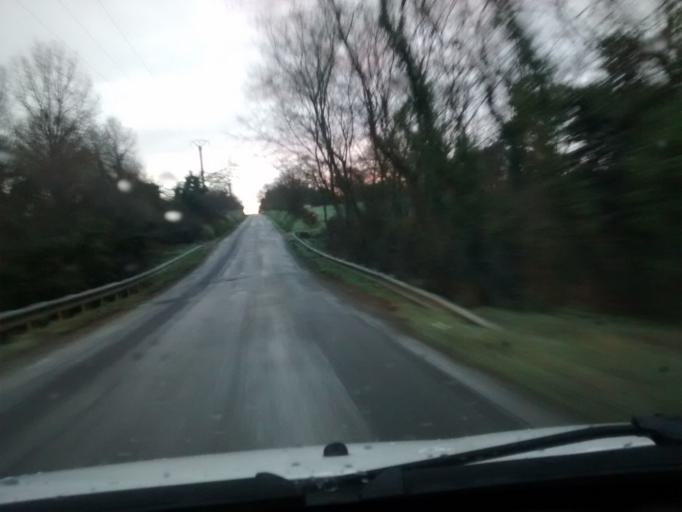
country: FR
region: Brittany
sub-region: Departement d'Ille-et-Vilaine
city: Chateaubourg
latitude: 48.0985
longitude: -1.3968
